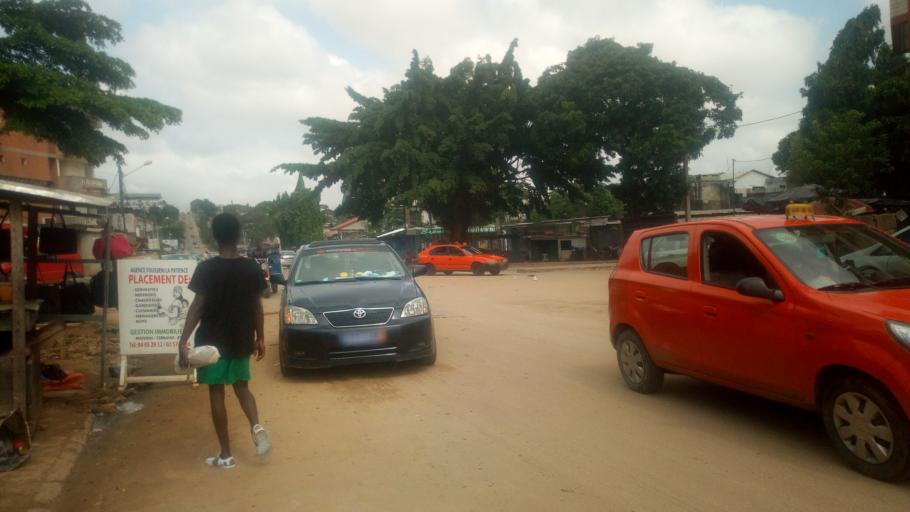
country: CI
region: Lagunes
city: Abidjan
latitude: 5.3638
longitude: -3.9614
